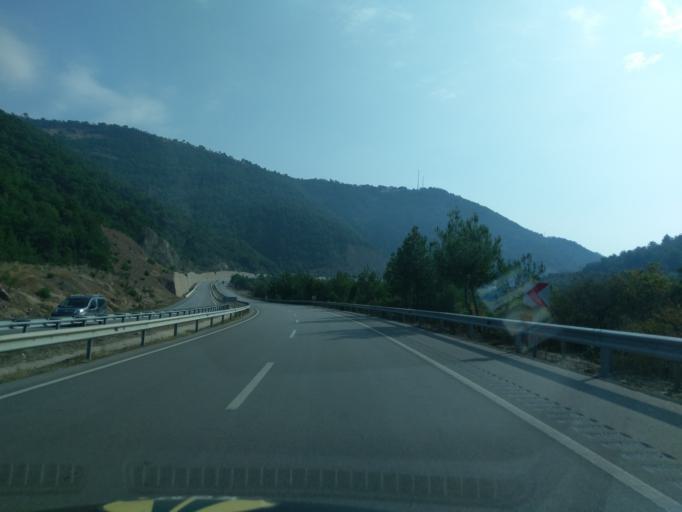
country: TR
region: Amasya
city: Akdag
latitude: 40.7517
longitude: 36.0784
